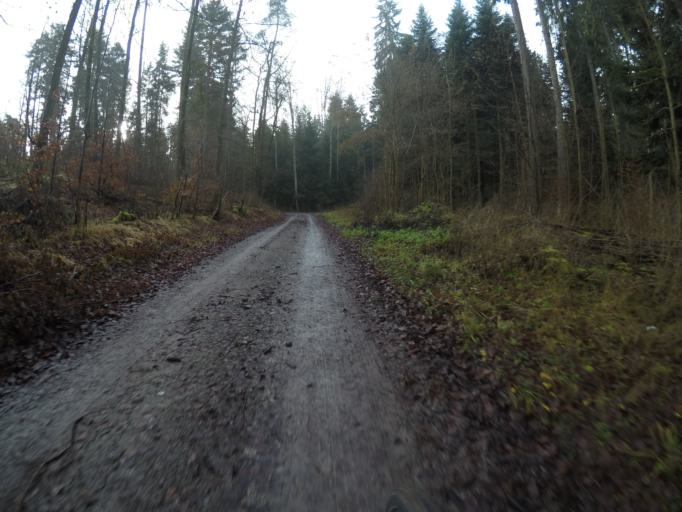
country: DE
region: Baden-Wuerttemberg
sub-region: Regierungsbezirk Stuttgart
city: Deckenpfronn
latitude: 48.6656
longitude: 8.8270
